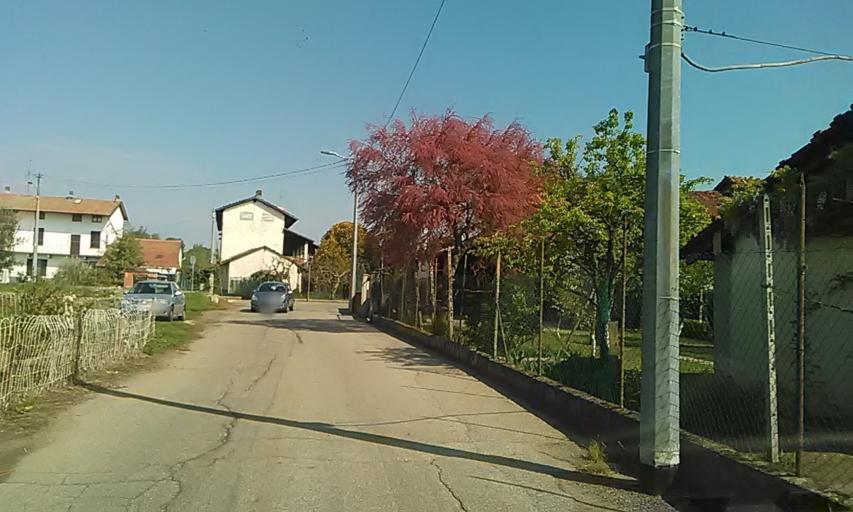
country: IT
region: Piedmont
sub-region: Provincia di Vercelli
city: Ghislarengo
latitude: 45.5300
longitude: 8.3846
